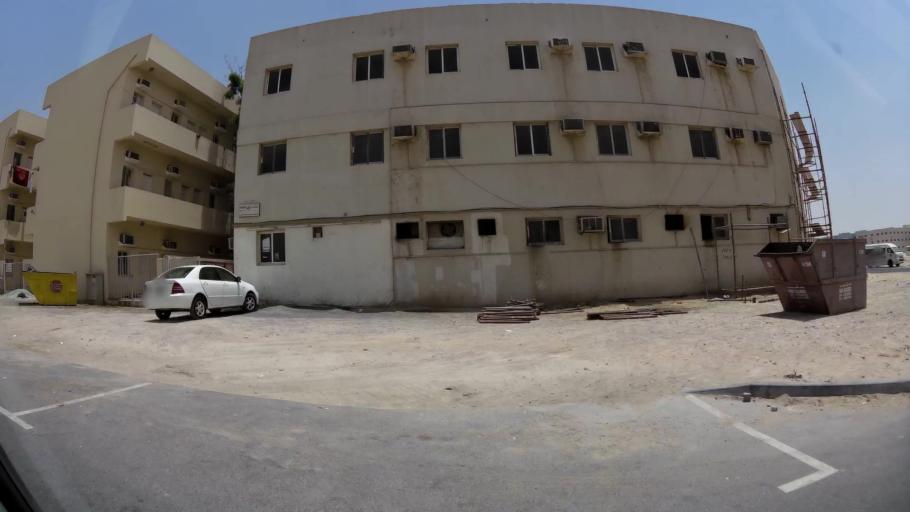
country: AE
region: Ash Shariqah
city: Sharjah
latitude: 25.2729
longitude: 55.4234
